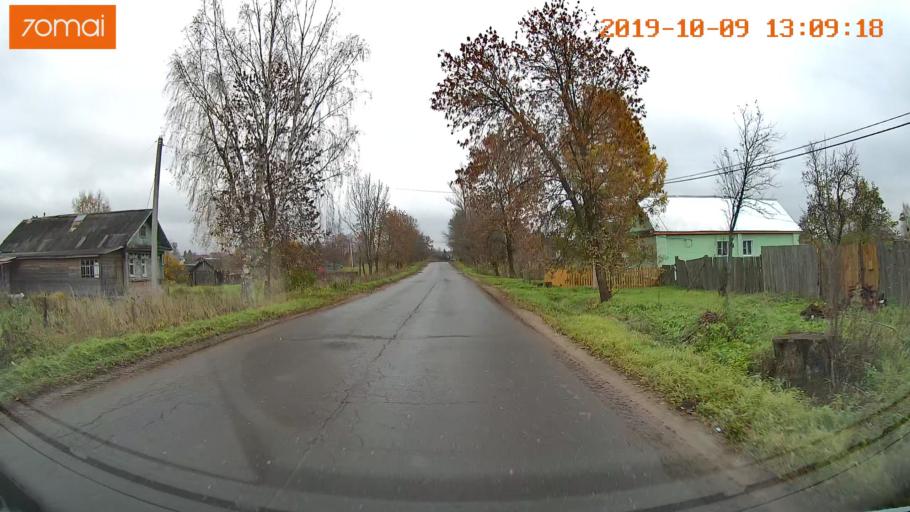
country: RU
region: Jaroslavl
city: Lyubim
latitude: 58.3572
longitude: 40.6742
